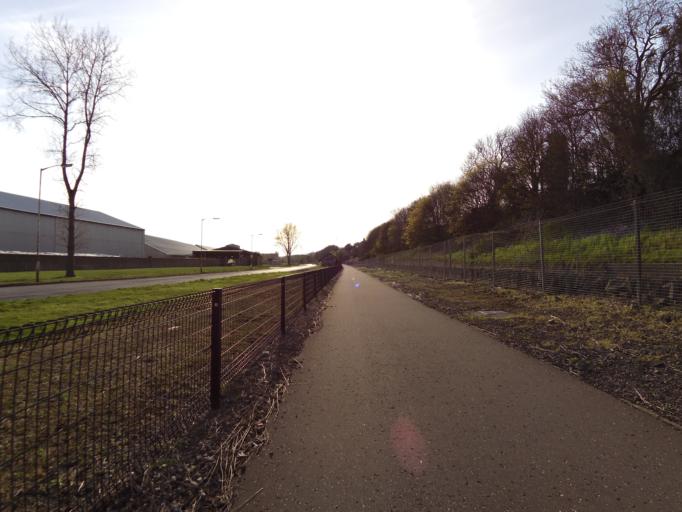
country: GB
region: Scotland
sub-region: Fife
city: Newport-On-Tay
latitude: 56.4681
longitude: -2.9291
